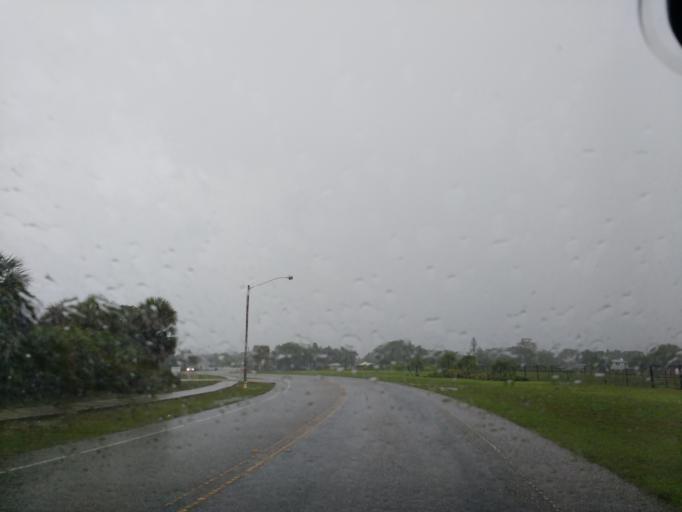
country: US
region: Florida
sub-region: Sarasota County
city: Venice
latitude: 27.0771
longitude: -82.4494
